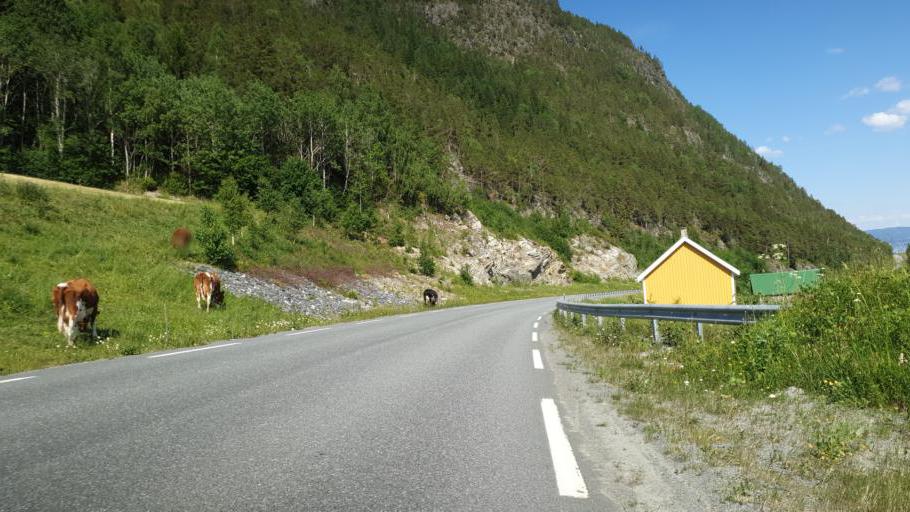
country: NO
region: Nord-Trondelag
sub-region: Leksvik
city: Leksvik
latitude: 63.6254
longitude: 10.5401
